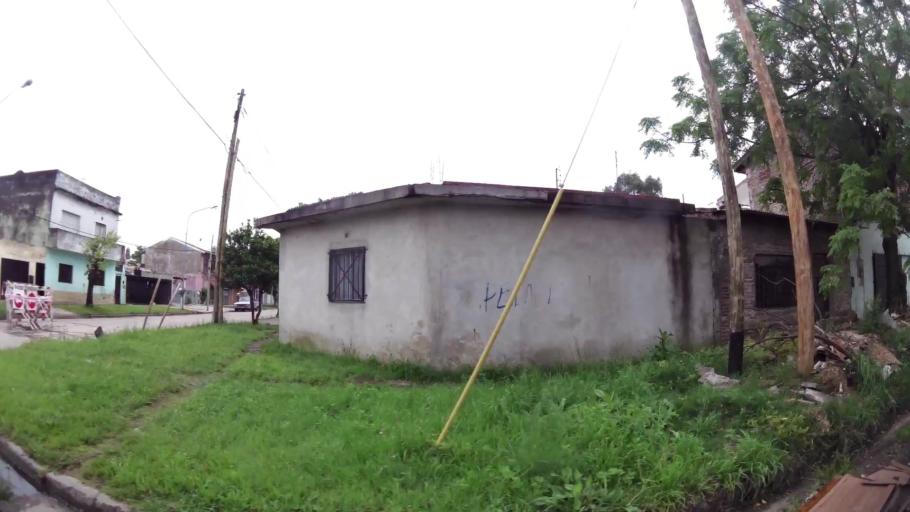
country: AR
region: Buenos Aires
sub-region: Partido de Lanus
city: Lanus
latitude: -34.7309
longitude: -58.3692
